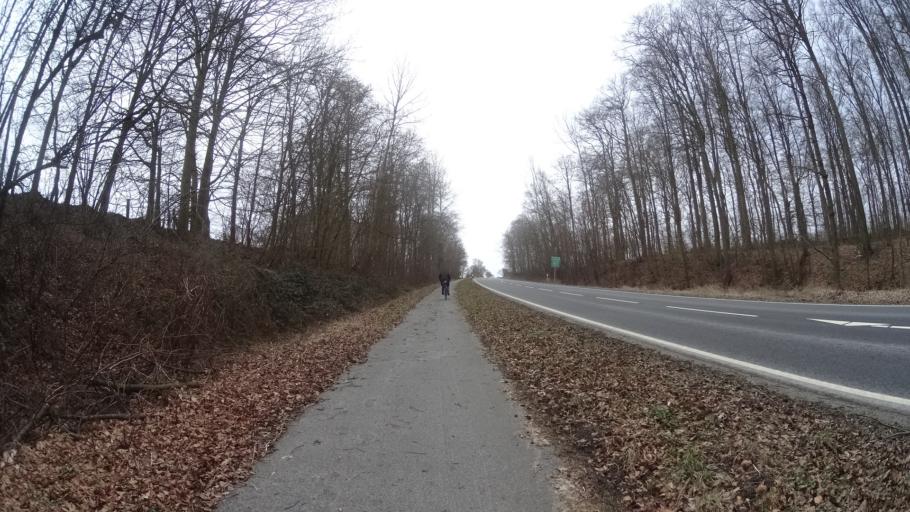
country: DE
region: Schleswig-Holstein
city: Hohenfelde
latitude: 54.3693
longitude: 10.5098
